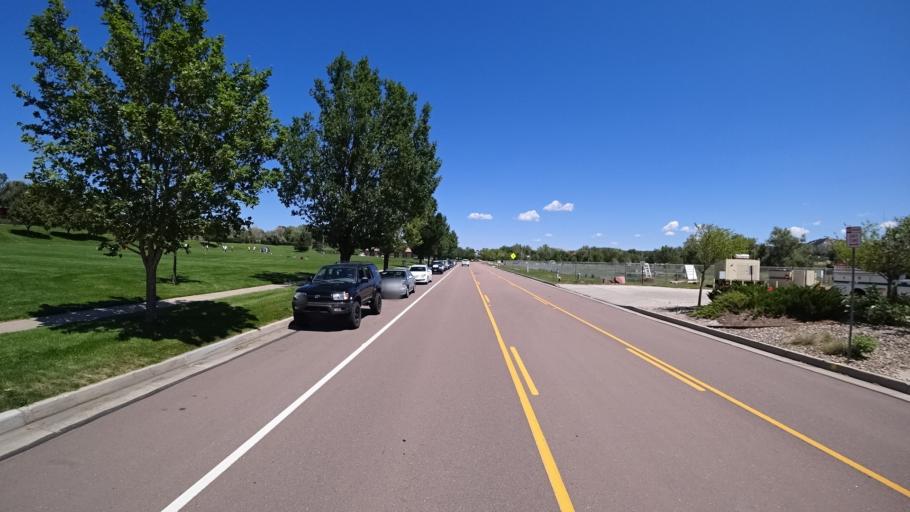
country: US
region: Colorado
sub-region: El Paso County
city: Colorado Springs
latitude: 38.8871
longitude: -104.8283
